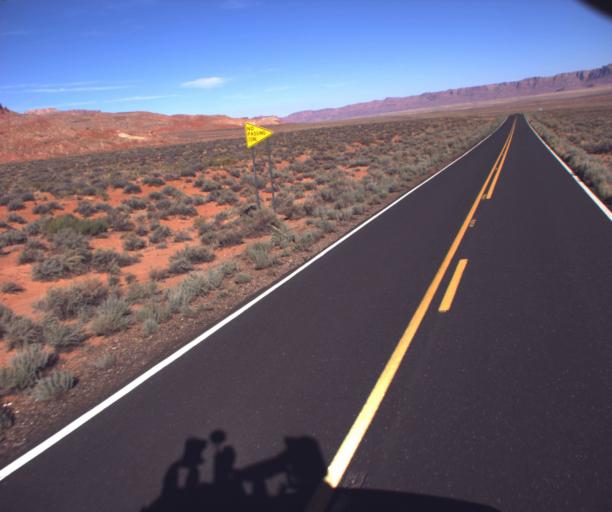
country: US
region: Arizona
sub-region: Coconino County
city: LeChee
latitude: 36.6858
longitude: -111.8355
